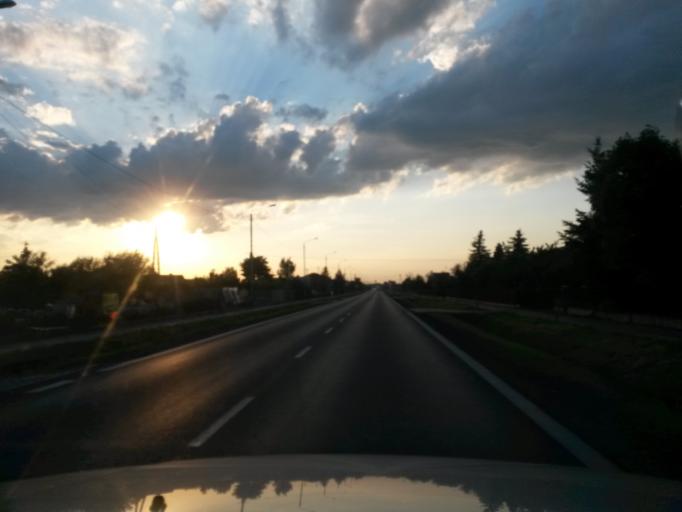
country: PL
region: Lodz Voivodeship
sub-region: Powiat wielunski
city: Wielun
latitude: 51.2342
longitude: 18.5375
